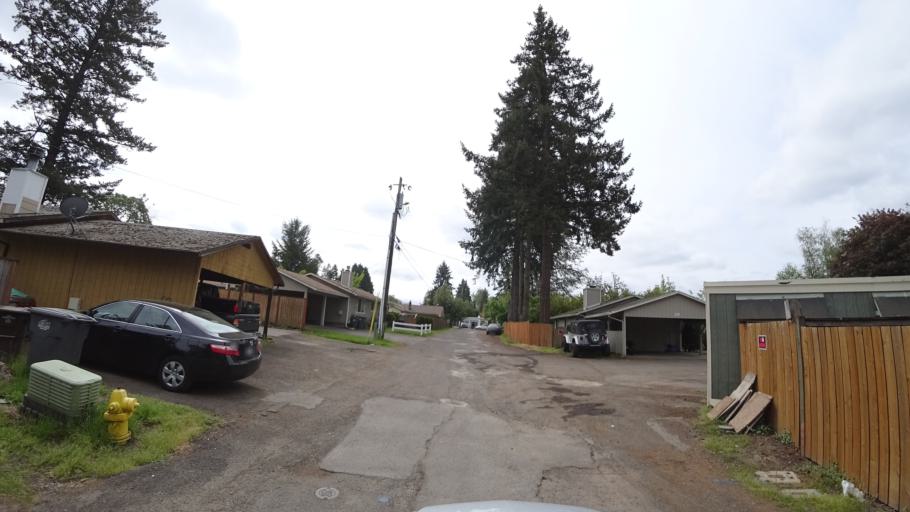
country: US
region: Oregon
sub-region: Washington County
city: Hillsboro
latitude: 45.5294
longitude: -122.9918
